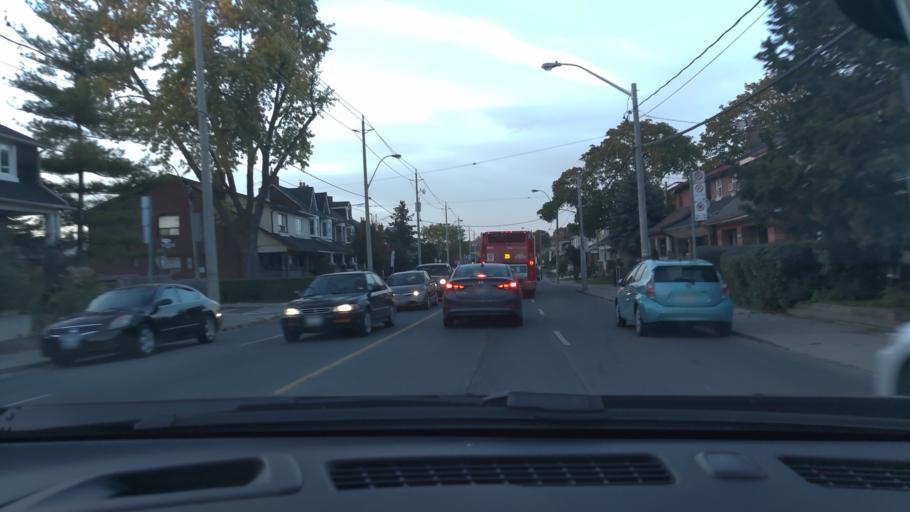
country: CA
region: Ontario
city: Toronto
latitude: 43.6808
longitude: -79.4441
